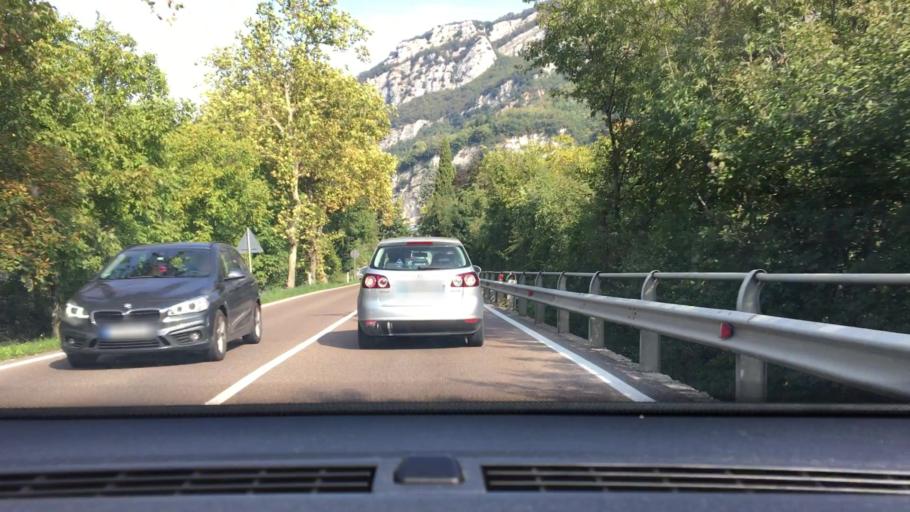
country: IT
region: Trentino-Alto Adige
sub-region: Provincia di Trento
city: Nago-Torbole
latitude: 45.8722
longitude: 10.9076
